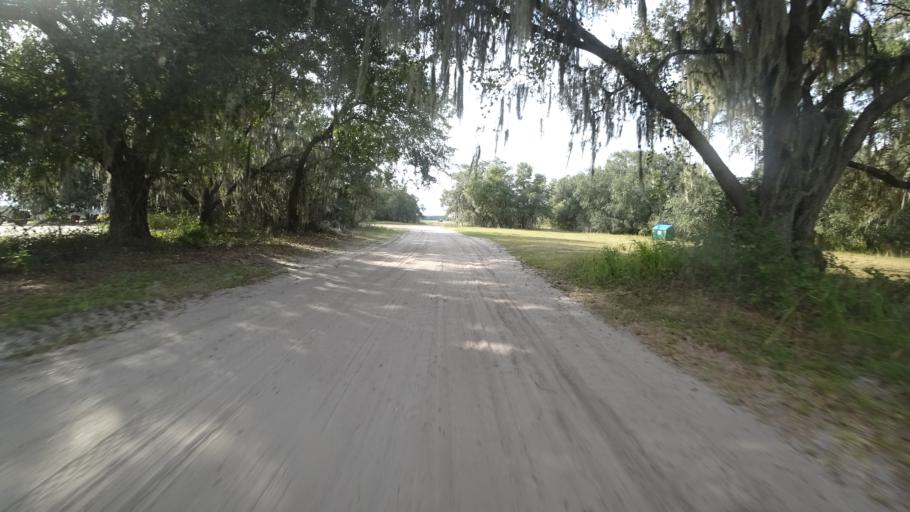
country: US
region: Florida
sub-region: Hillsborough County
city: Wimauma
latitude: 27.6012
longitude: -82.1340
